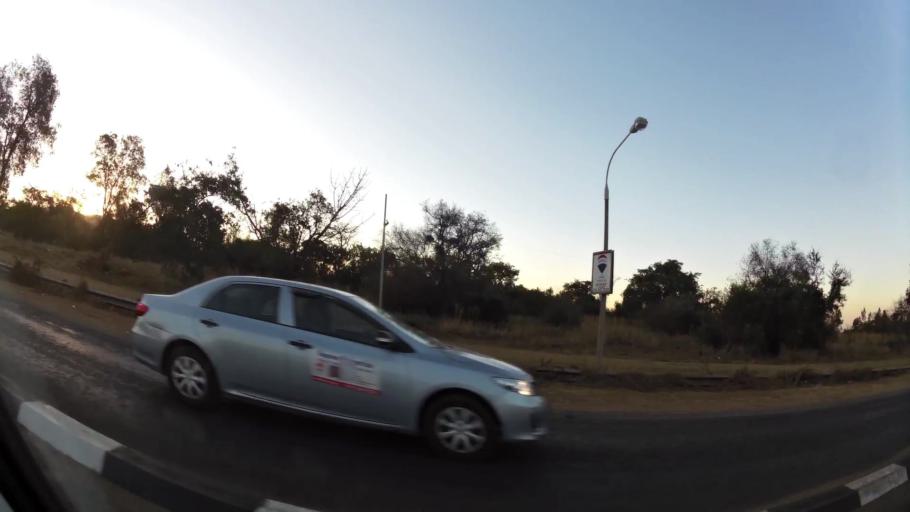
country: ZA
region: North-West
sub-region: Bojanala Platinum District Municipality
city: Rustenburg
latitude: -25.6709
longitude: 27.2187
